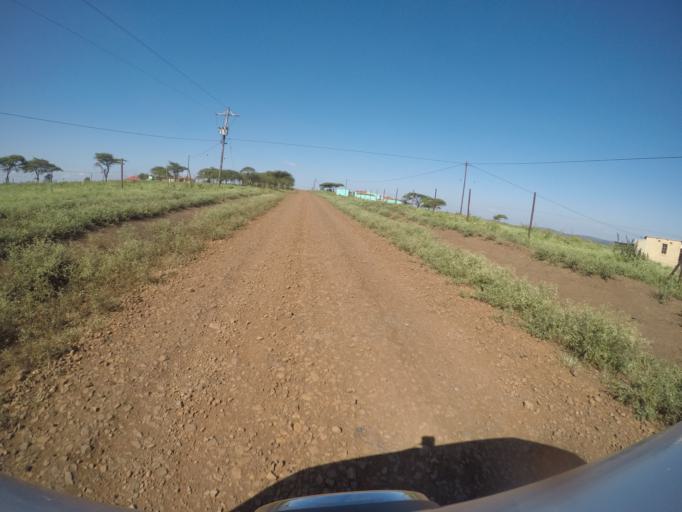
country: ZA
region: KwaZulu-Natal
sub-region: uThungulu District Municipality
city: Empangeni
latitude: -28.5717
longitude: 31.7310
